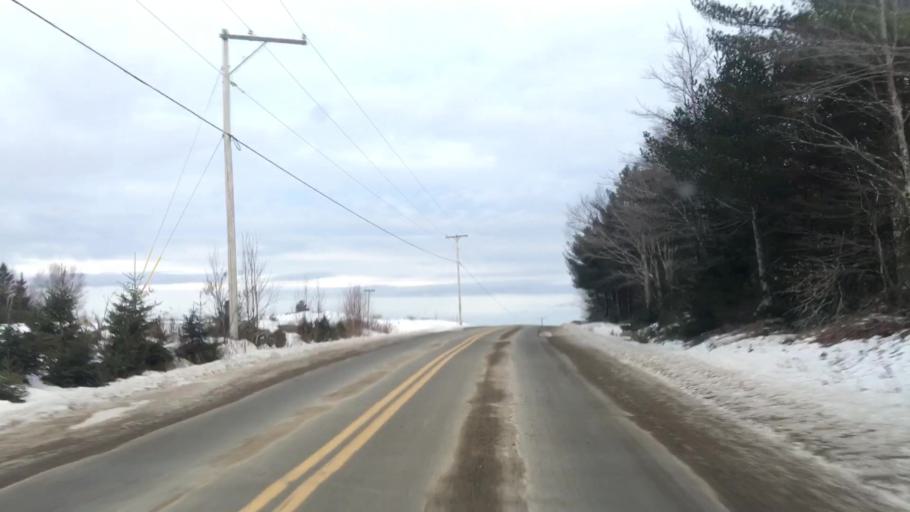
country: US
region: Maine
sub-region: Hancock County
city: Franklin
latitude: 44.8443
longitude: -68.3272
